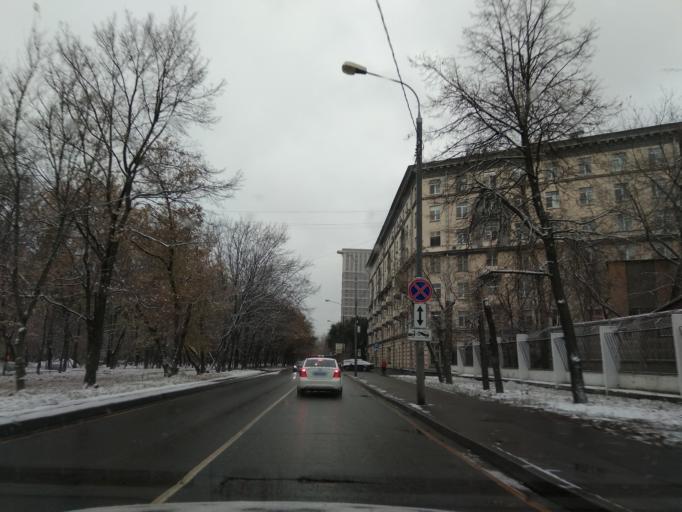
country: RU
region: Moskovskaya
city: Khoroshevo-Mnevniki
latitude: 55.7886
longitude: 37.4818
